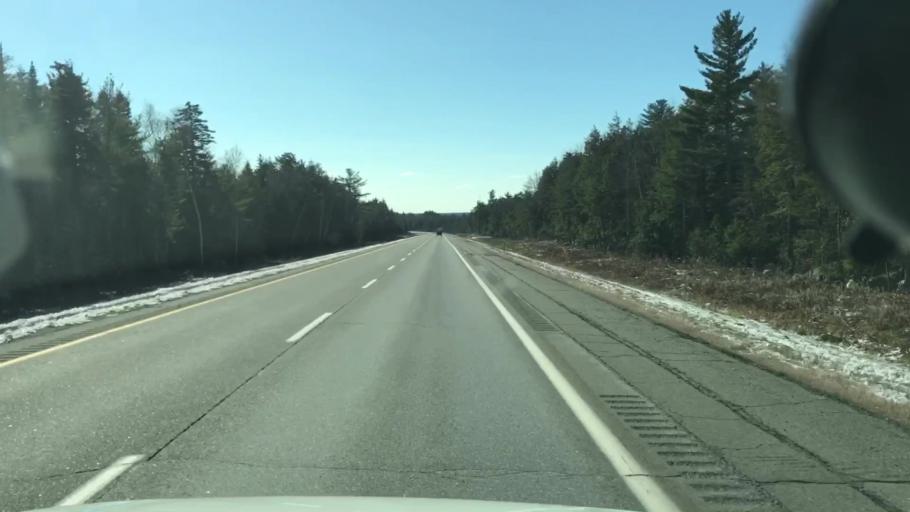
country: US
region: Maine
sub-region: Penobscot County
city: Howland
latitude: 45.2798
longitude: -68.6727
